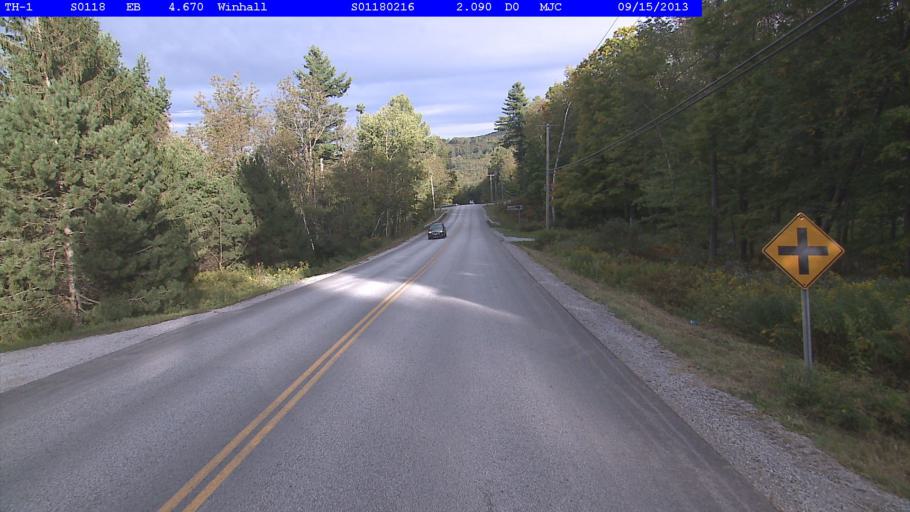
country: US
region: Vermont
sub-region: Bennington County
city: Manchester Center
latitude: 43.1356
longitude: -72.8928
